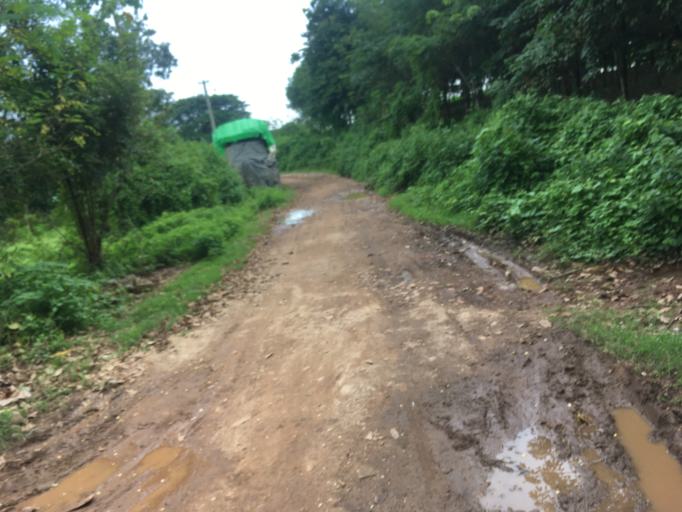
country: MM
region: Mon
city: Mawlamyine
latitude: 16.4592
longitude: 97.6655
